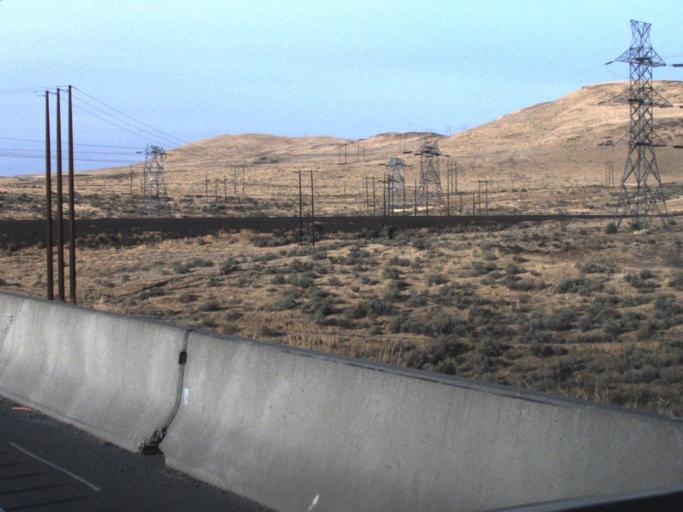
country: US
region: Oregon
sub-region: Umatilla County
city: Umatilla
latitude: 45.9361
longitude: -119.3307
